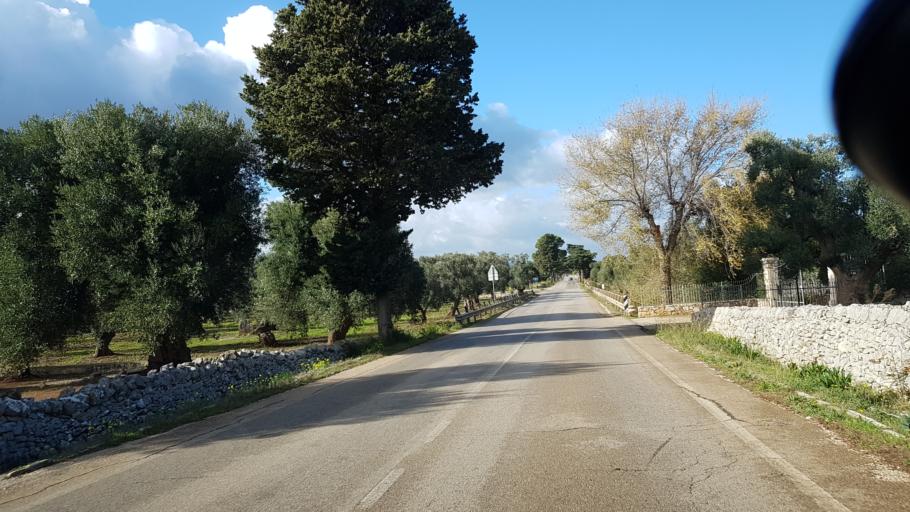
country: IT
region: Apulia
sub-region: Provincia di Brindisi
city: Pezze di Greco
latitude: 40.7968
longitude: 17.4486
